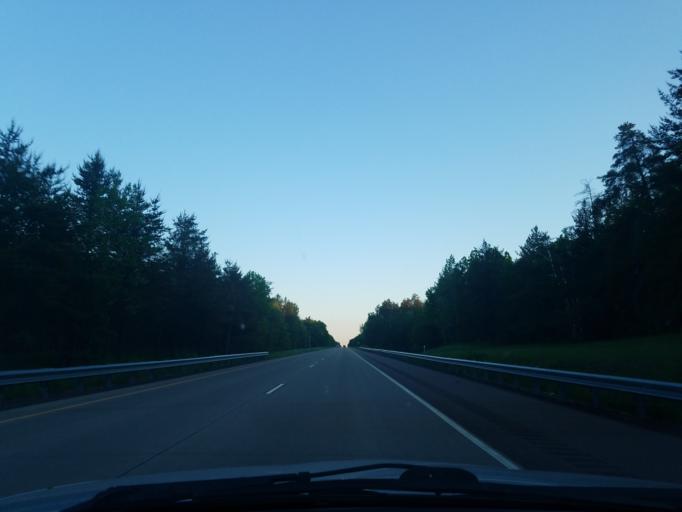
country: US
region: Minnesota
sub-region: Pine County
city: Sandstone
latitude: 46.2156
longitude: -92.8372
